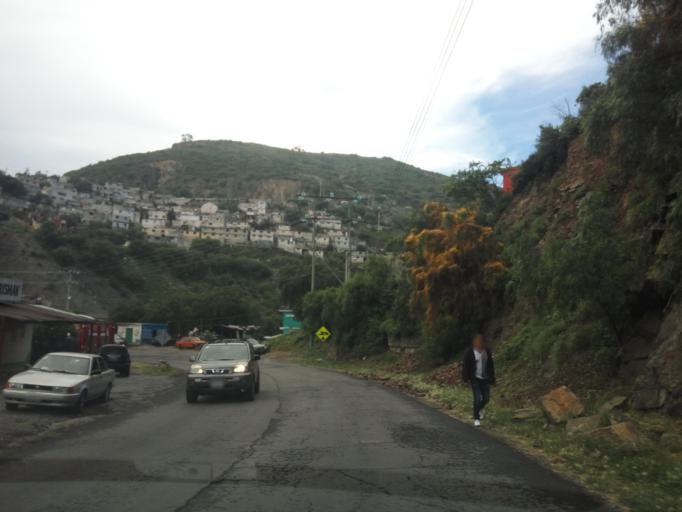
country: MX
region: Hidalgo
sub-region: Pachuca de Soto
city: Camelia (Barrio la Camelia)
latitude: 20.1360
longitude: -98.7238
